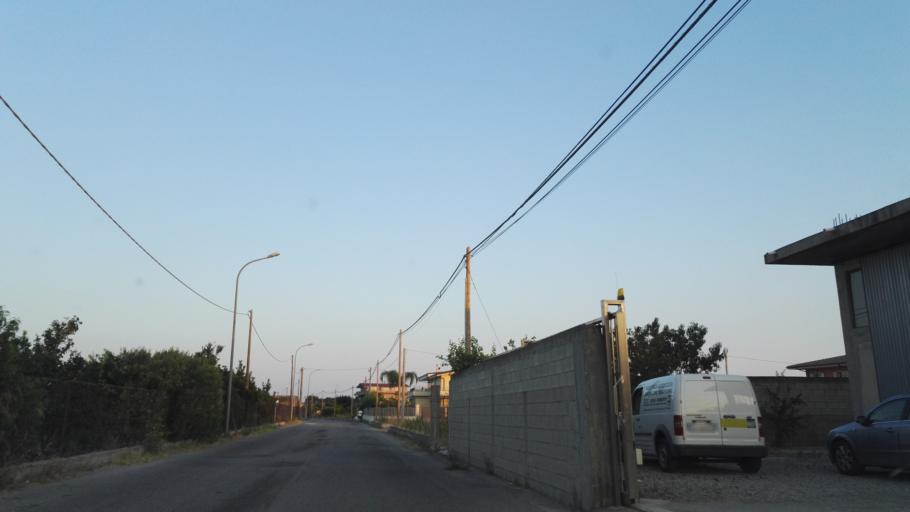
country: IT
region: Calabria
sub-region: Provincia di Reggio Calabria
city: Caulonia Marina
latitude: 38.3541
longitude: 16.4705
